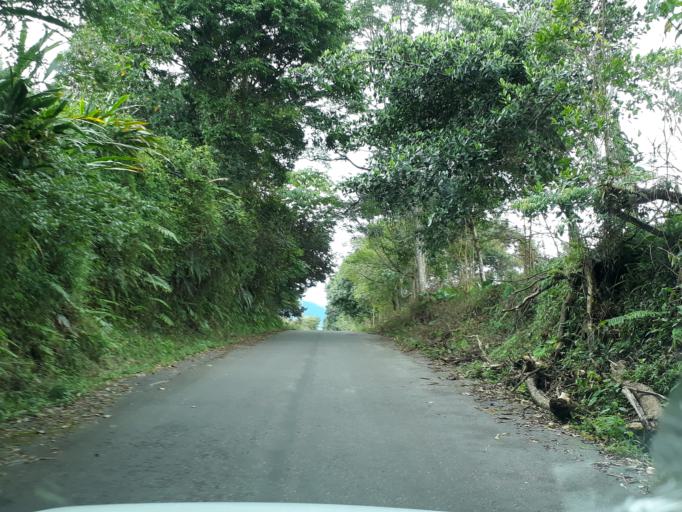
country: CO
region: Cundinamarca
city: Medina
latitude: 4.5774
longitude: -73.3559
